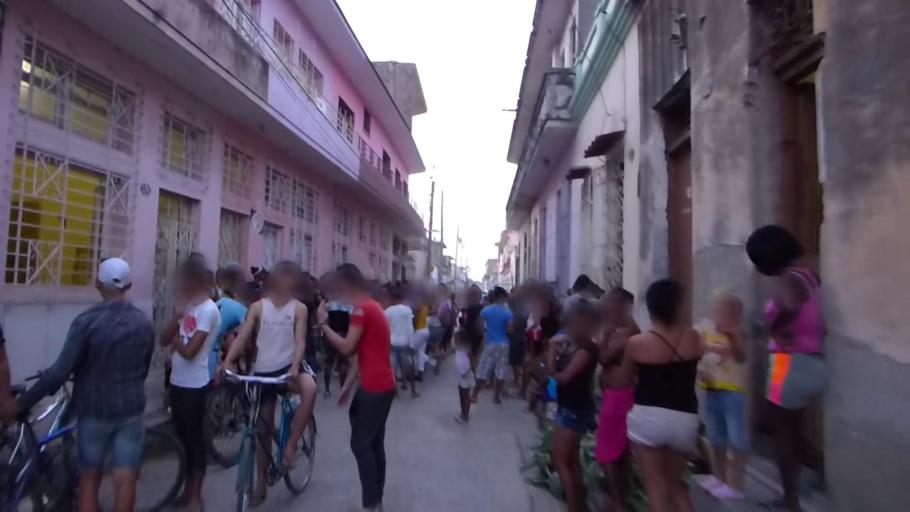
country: CU
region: Camaguey
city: Camaguey
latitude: 21.3756
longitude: -77.9202
